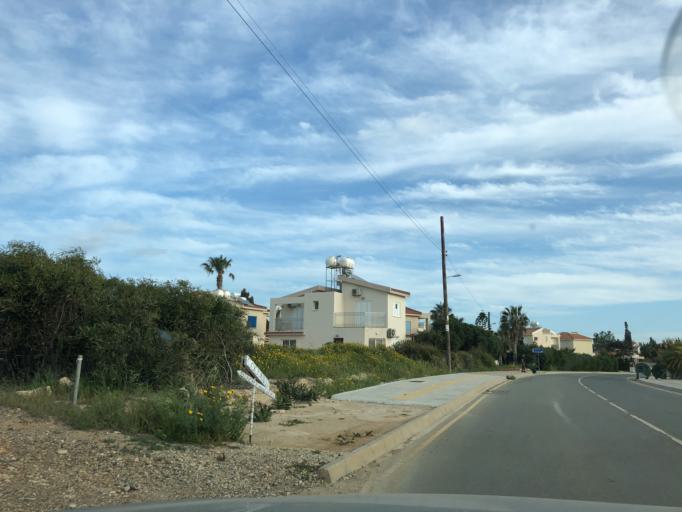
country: CY
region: Larnaka
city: Perivolia
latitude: 34.8205
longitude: 33.6014
